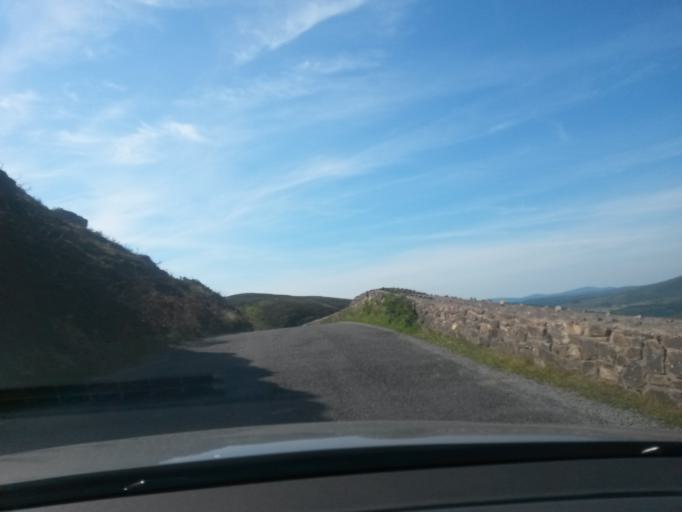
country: IE
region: Leinster
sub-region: Wicklow
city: Enniskerry
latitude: 53.1098
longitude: -6.2580
